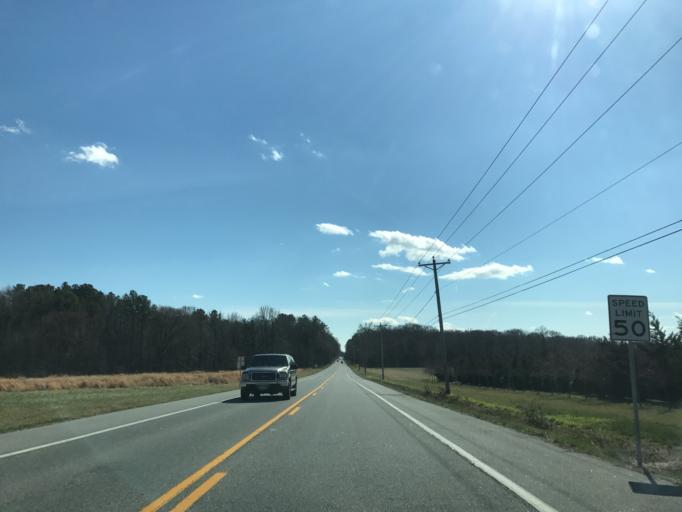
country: US
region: Maryland
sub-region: Kent County
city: Rock Hall
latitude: 39.1977
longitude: -76.1899
